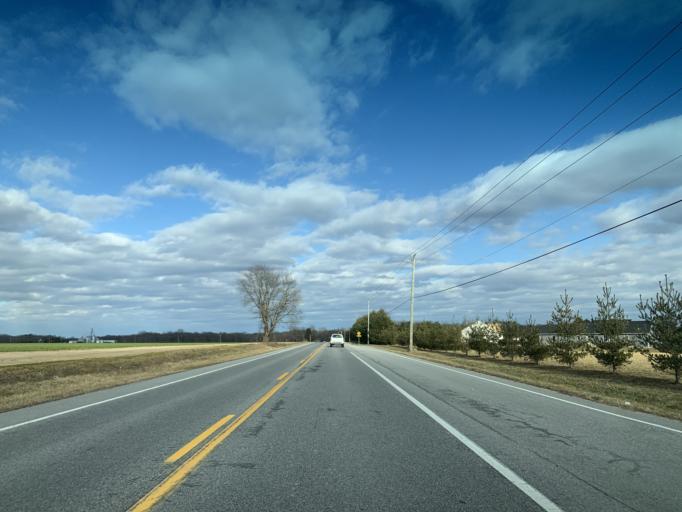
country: US
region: Maryland
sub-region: Caroline County
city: Ridgely
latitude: 39.0311
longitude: -75.8932
